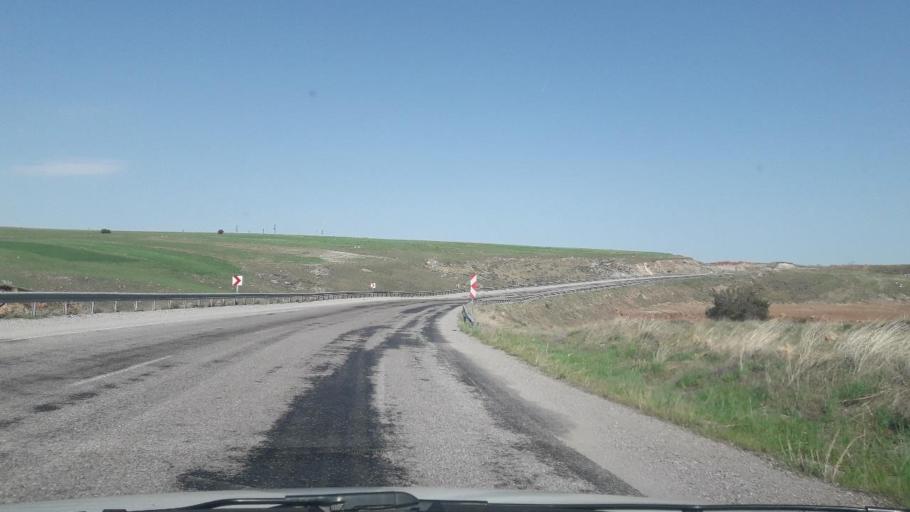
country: TR
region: Sivas
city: Kangal
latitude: 39.1659
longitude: 37.4736
